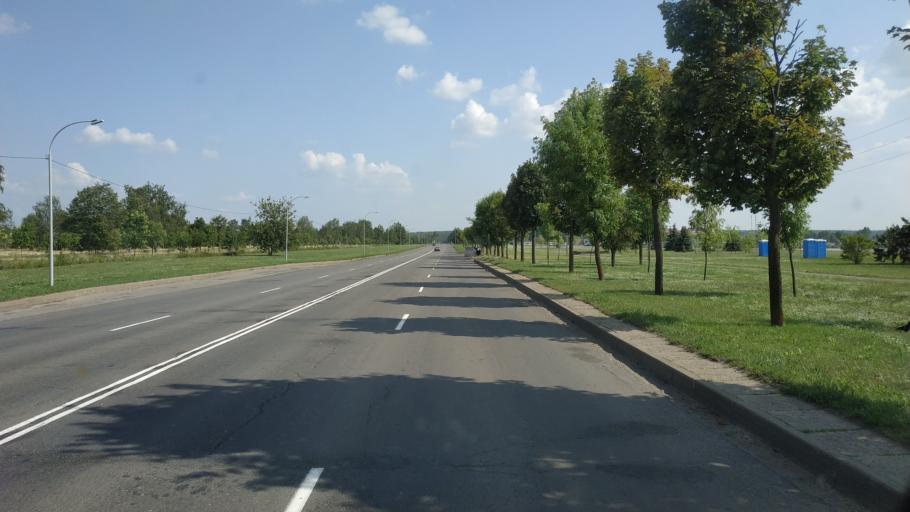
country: BY
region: Mogilev
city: Buynichy
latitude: 53.8627
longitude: 30.3210
